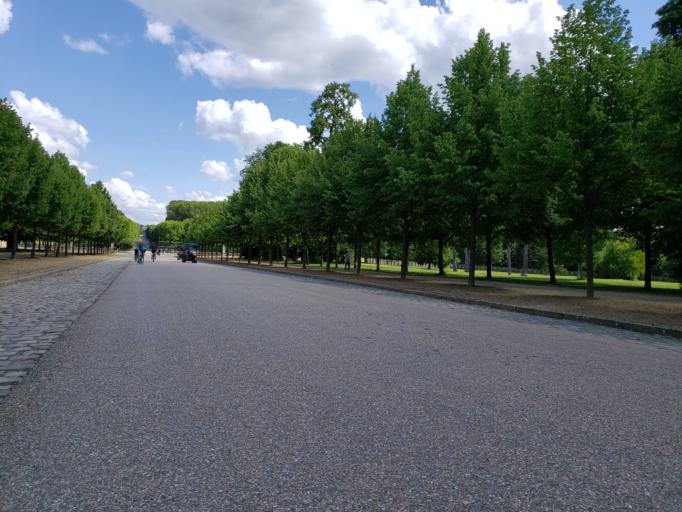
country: FR
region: Ile-de-France
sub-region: Departement des Yvelines
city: Le Chesnay
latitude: 48.8131
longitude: 2.1087
